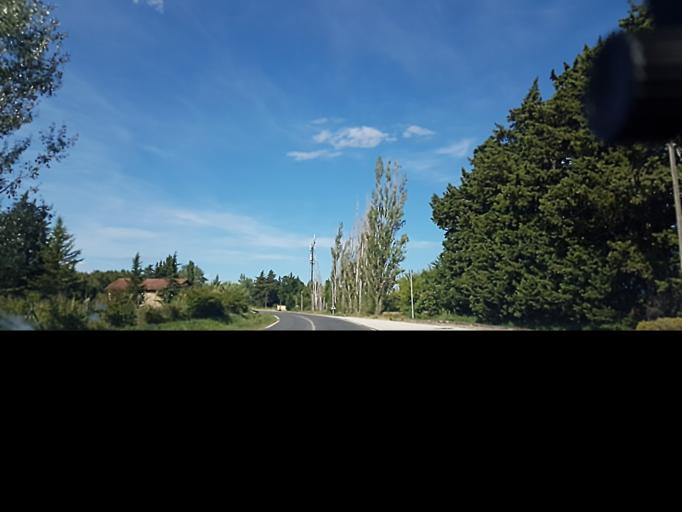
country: FR
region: Provence-Alpes-Cote d'Azur
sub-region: Departement du Vaucluse
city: Le Thor
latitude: 43.9196
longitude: 4.9820
